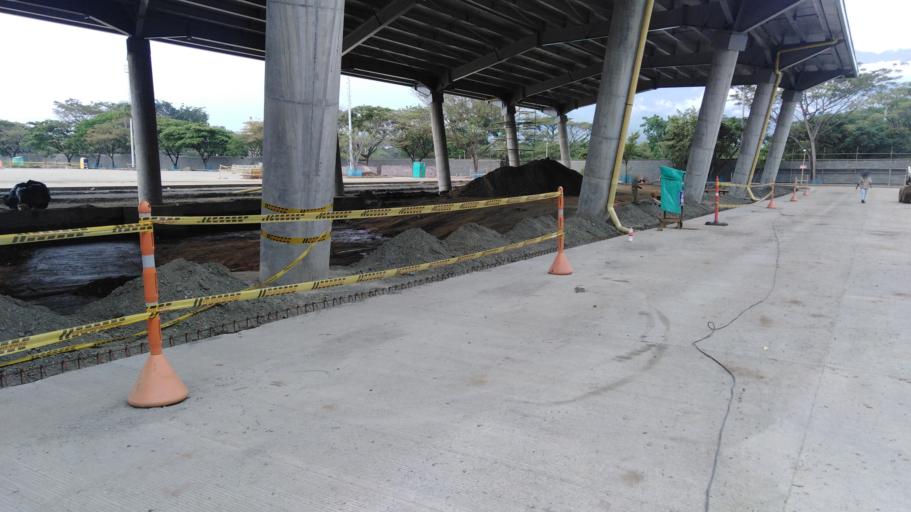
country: CO
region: Valle del Cauca
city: Cali
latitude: 3.3611
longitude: -76.5217
